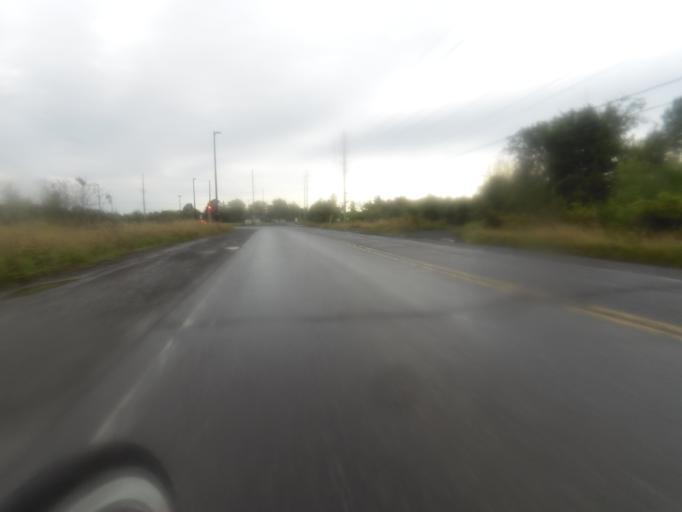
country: CA
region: Ontario
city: Bells Corners
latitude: 45.2635
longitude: -75.7365
